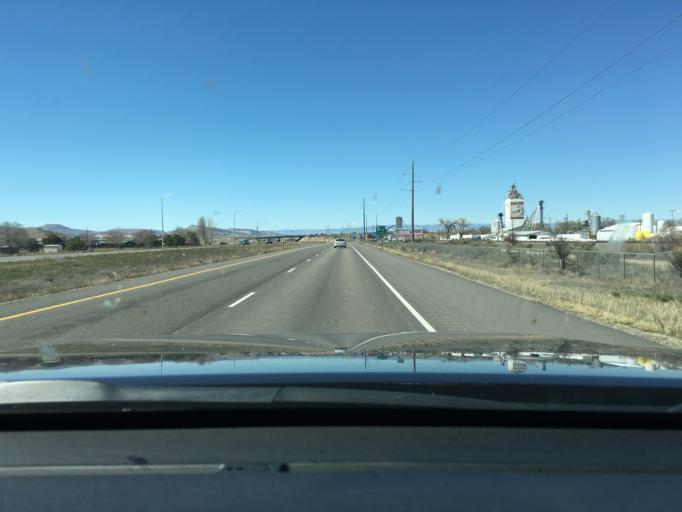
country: US
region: Colorado
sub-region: Mesa County
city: Fruita
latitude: 39.1521
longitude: -108.7290
